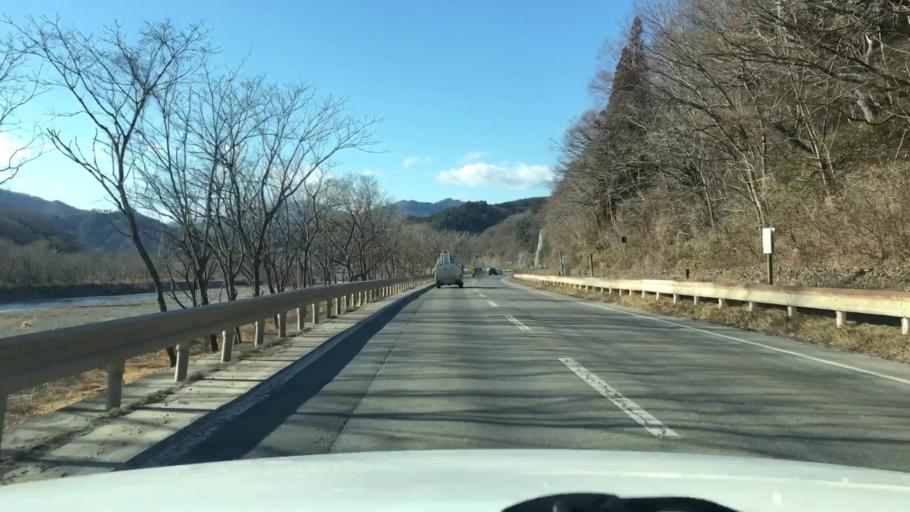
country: JP
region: Iwate
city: Miyako
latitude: 39.6311
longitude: 141.8741
